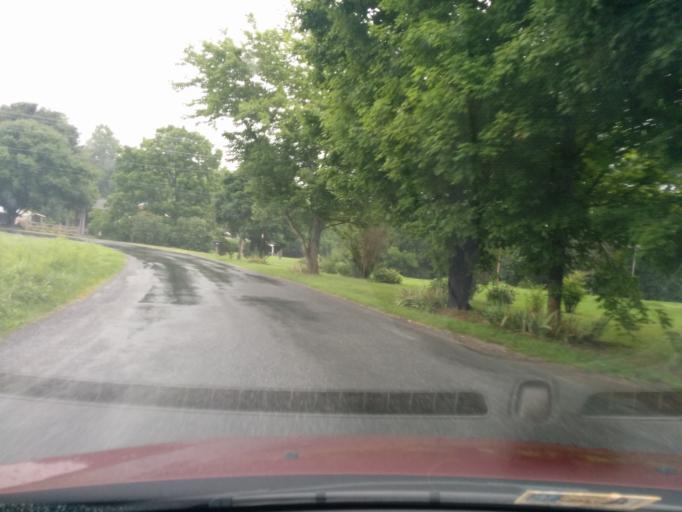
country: US
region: Virginia
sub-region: Rockbridge County
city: East Lexington
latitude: 37.8998
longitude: -79.4127
